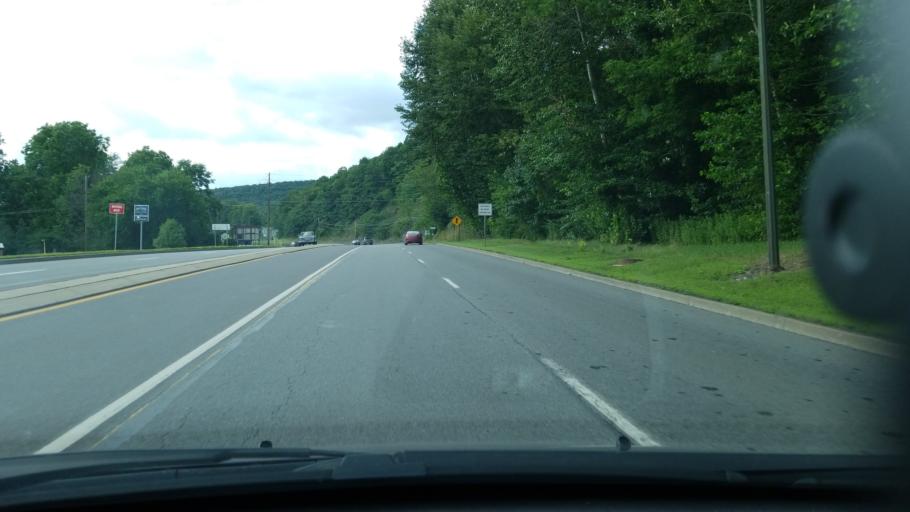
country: US
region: Pennsylvania
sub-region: Montour County
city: Danville
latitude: 40.9699
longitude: -76.6164
